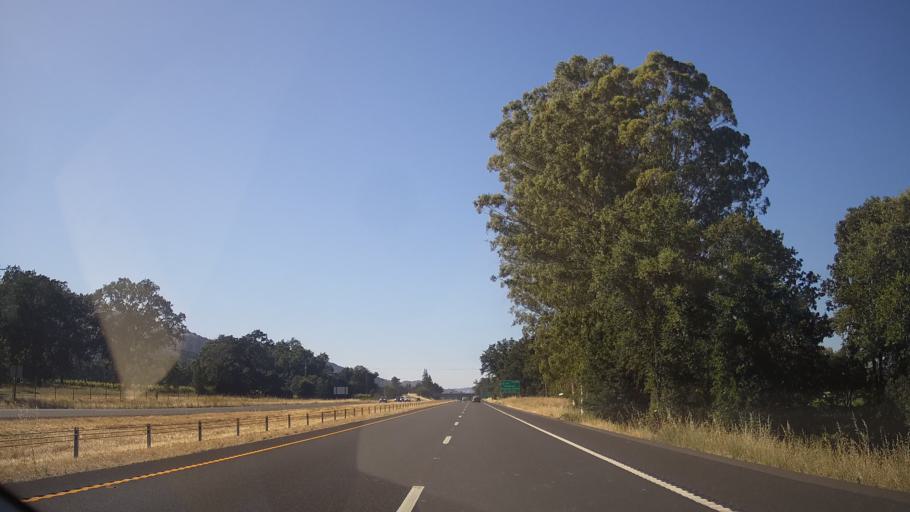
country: US
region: California
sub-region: Mendocino County
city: Talmage
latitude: 39.0915
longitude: -123.1863
